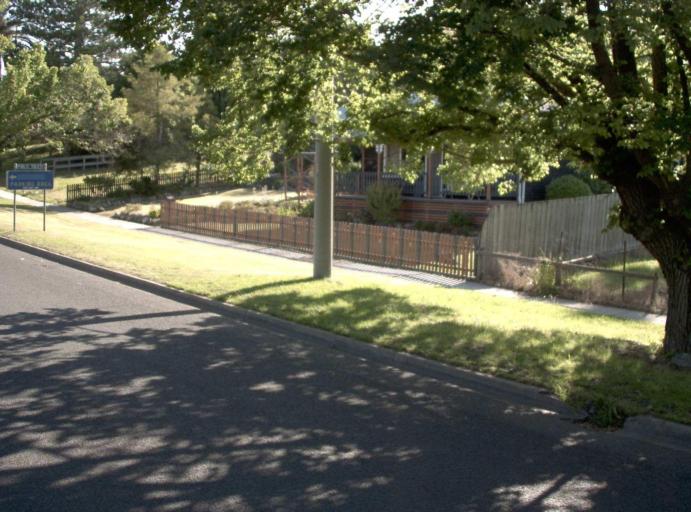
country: AU
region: Victoria
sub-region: East Gippsland
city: Lakes Entrance
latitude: -37.7098
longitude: 148.4535
